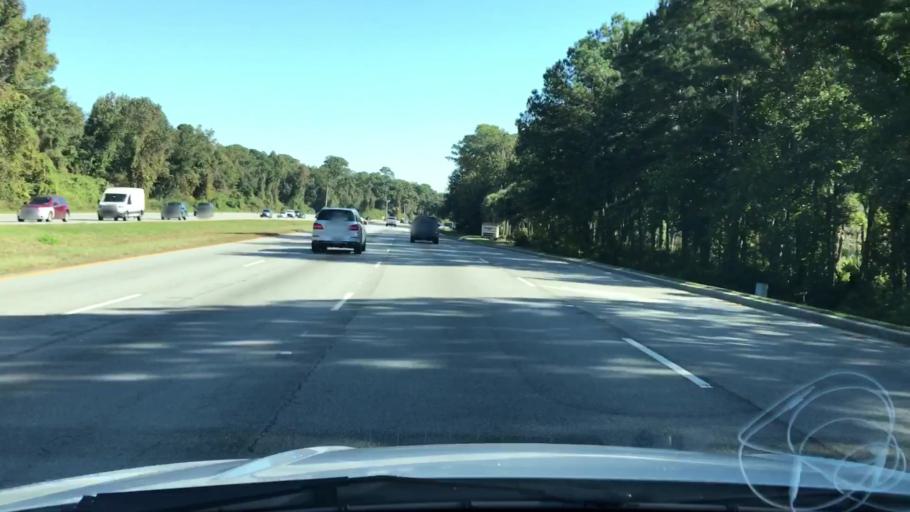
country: US
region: South Carolina
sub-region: Beaufort County
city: Bluffton
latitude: 32.2410
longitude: -80.8203
